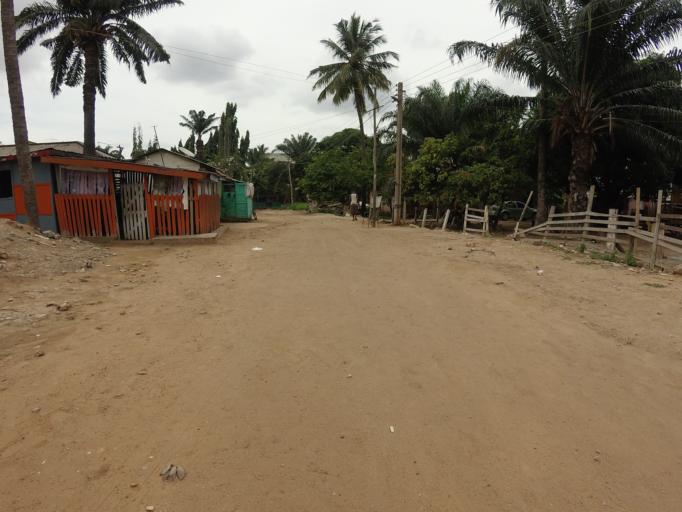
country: GH
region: Greater Accra
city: Accra
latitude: 5.5996
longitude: -0.2227
